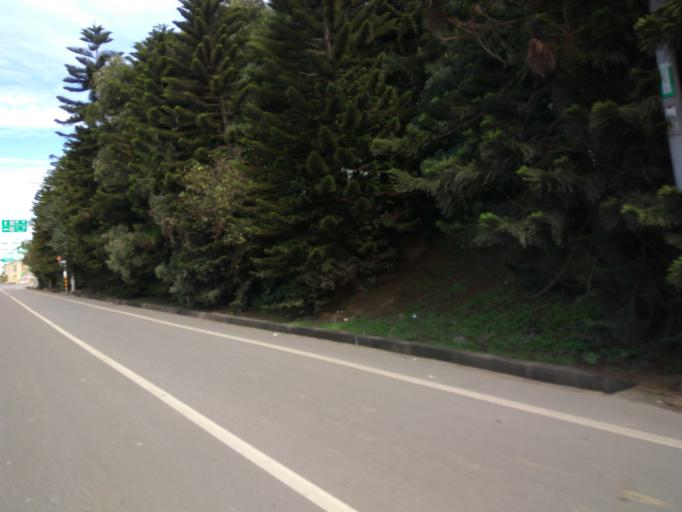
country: TW
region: Taiwan
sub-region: Hsinchu
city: Zhubei
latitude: 24.9893
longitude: 121.1026
